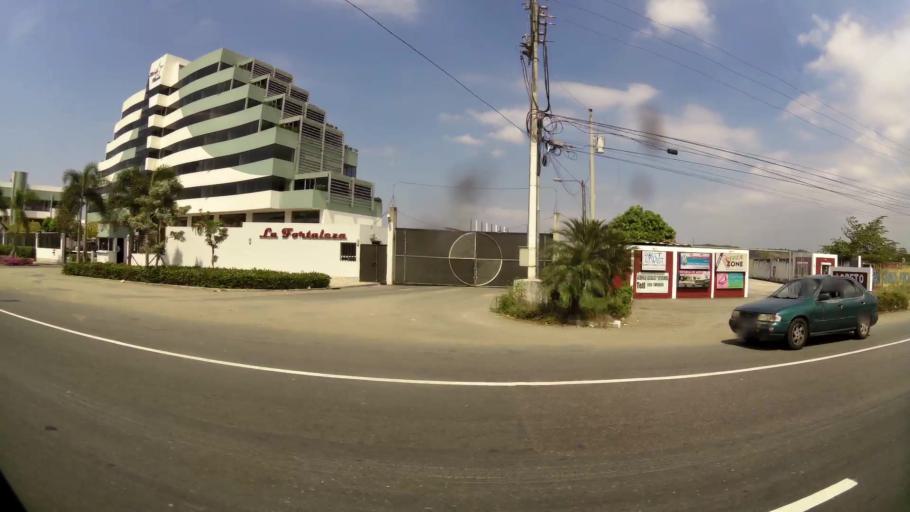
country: EC
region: Guayas
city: El Triunfo
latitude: -2.0505
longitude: -79.9134
